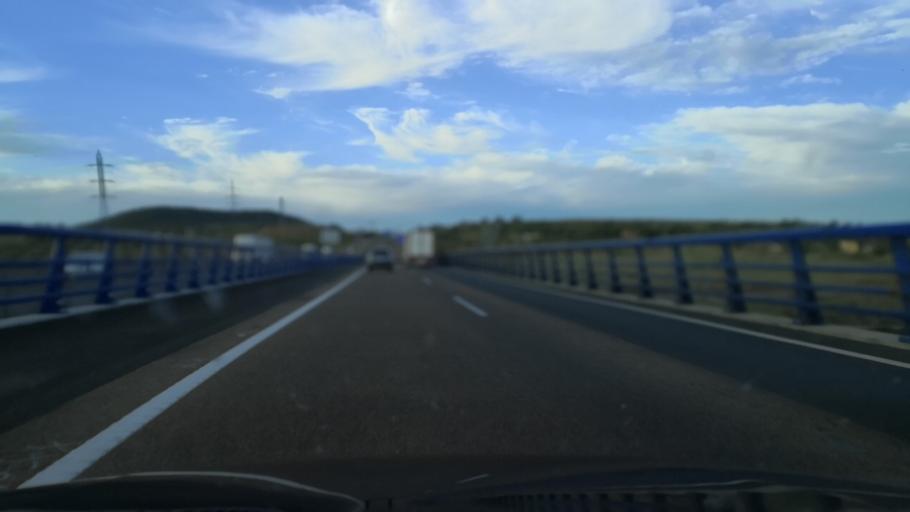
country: ES
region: Extremadura
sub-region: Provincia de Badajoz
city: Merida
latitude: 38.9287
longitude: -6.3685
